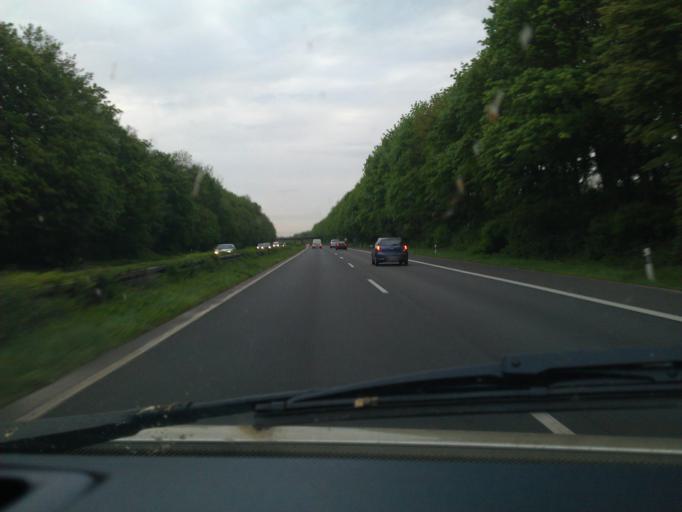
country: DE
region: North Rhine-Westphalia
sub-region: Regierungsbezirk Koln
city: Aldenhoven
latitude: 50.9074
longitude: 6.3108
